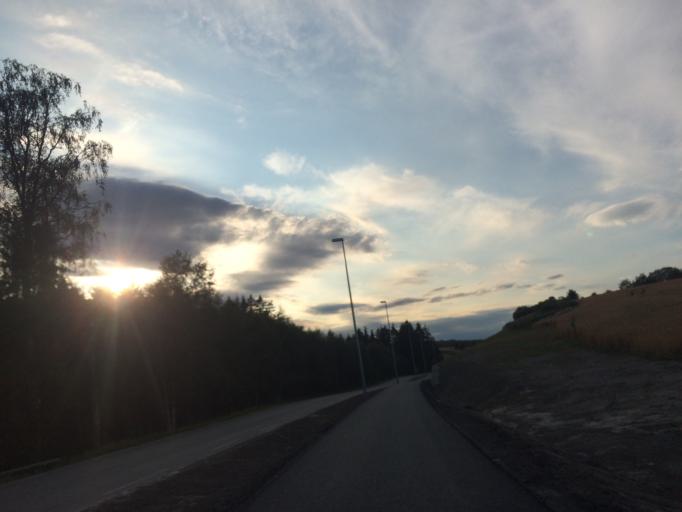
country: NO
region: Akershus
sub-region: Ski
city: Ski
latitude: 59.6843
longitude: 10.8727
